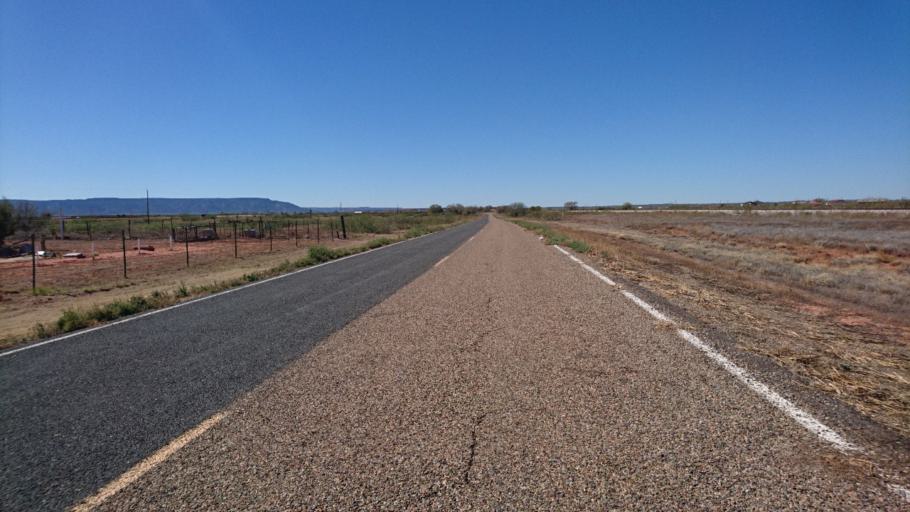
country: US
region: New Mexico
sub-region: Quay County
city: Tucumcari
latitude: 35.0990
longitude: -104.0548
